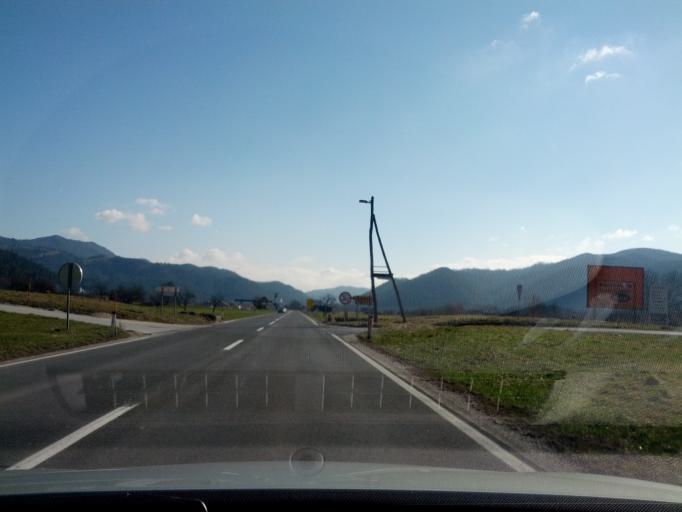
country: SI
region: Dol pri Ljubljani
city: Dol pri Ljubljani
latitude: 46.0898
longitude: 14.6452
